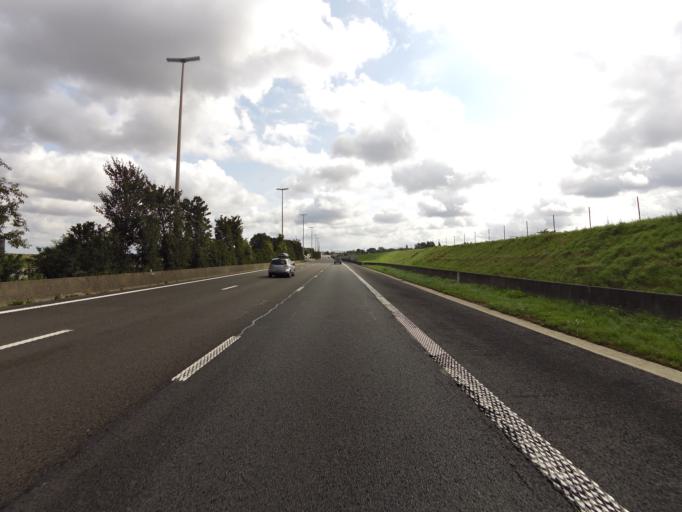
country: BE
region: Wallonia
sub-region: Province de Liege
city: Lincent
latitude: 50.7175
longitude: 5.0179
